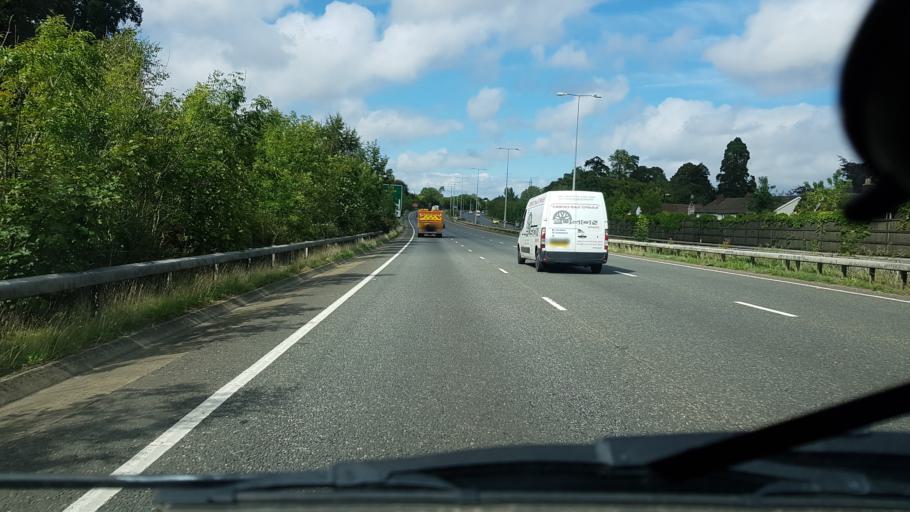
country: GB
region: England
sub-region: West Sussex
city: Broadfield
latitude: 51.0751
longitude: -0.2037
